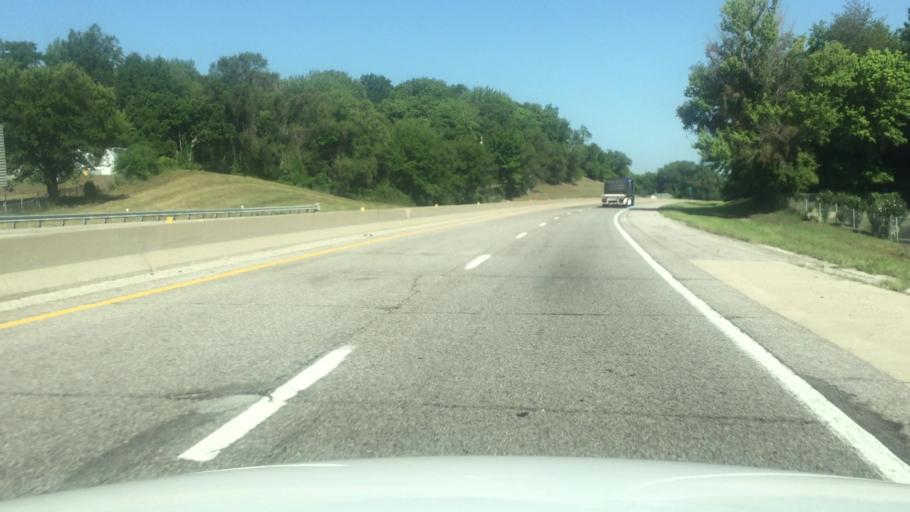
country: US
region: Kansas
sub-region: Doniphan County
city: Elwood
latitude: 39.7278
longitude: -94.8439
